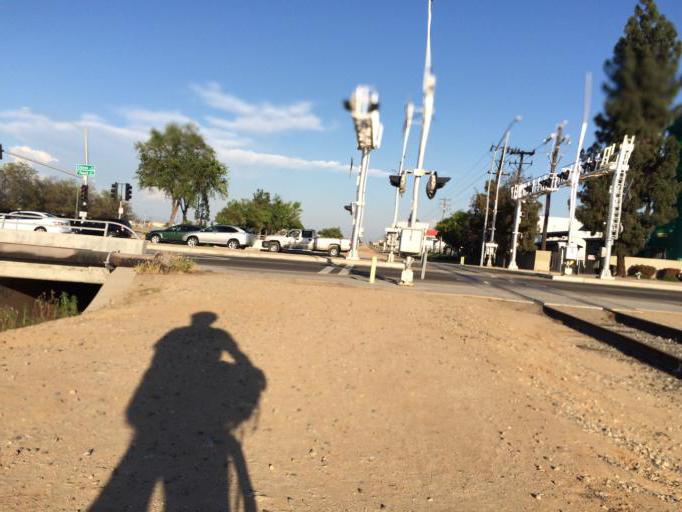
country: US
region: California
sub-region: Fresno County
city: Sunnyside
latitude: 36.7648
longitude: -119.7187
